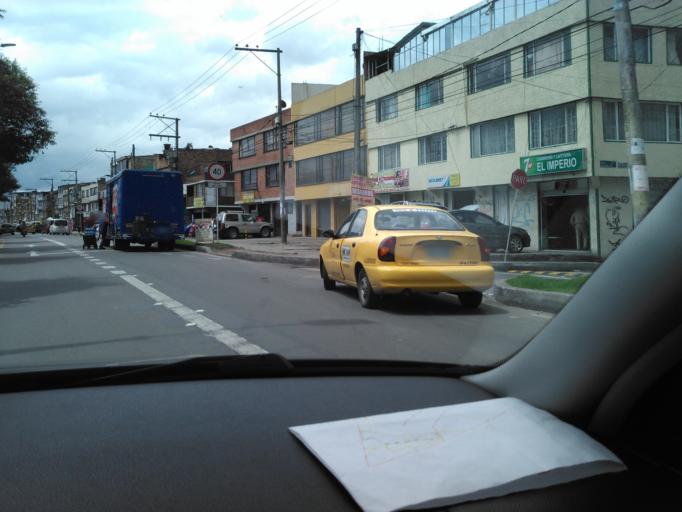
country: CO
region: Bogota D.C.
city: Bogota
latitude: 4.6188
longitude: -74.1130
